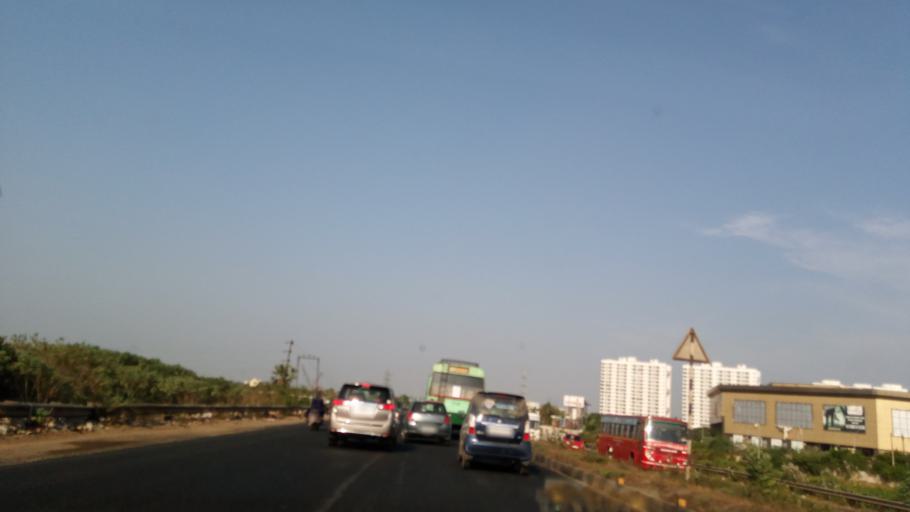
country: IN
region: Tamil Nadu
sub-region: Kancheepuram
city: Nandambakkam
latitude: 13.0360
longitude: 80.0441
